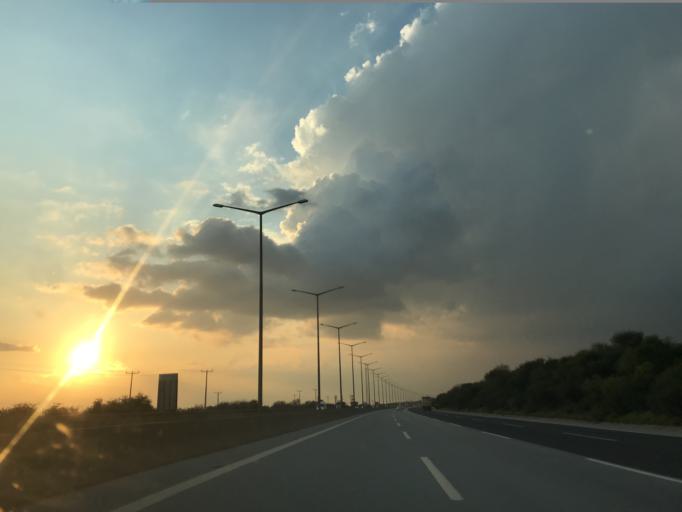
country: TR
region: Adana
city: Seyhan
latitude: 37.0306
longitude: 35.1954
